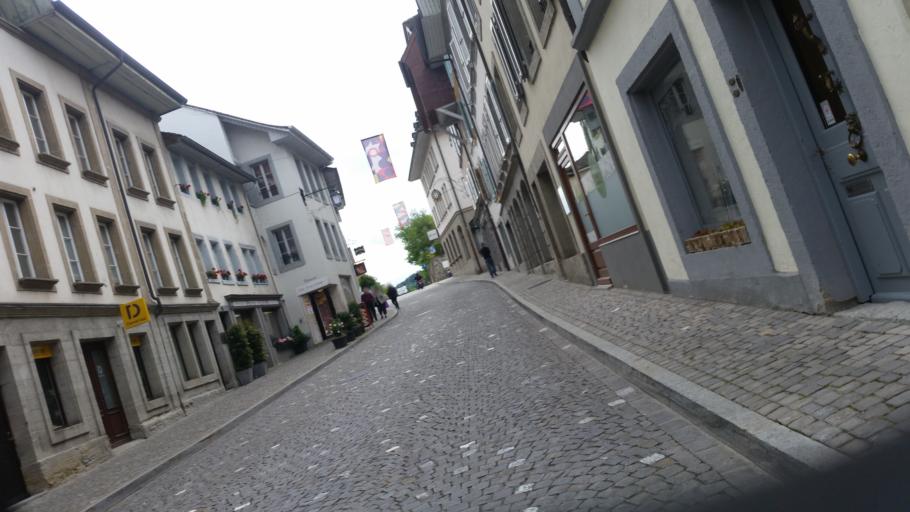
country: CH
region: Fribourg
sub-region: Broye District
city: Estavayer-le-Lac
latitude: 46.8487
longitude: 6.8464
